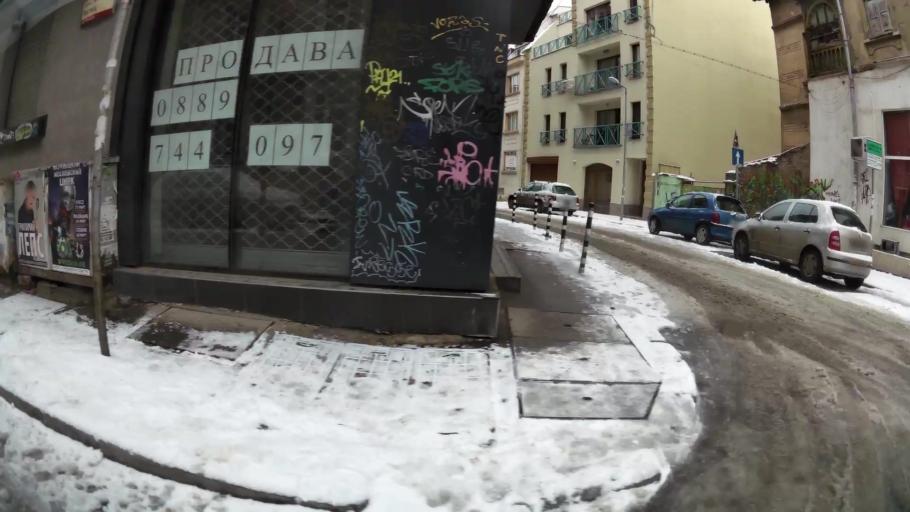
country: BG
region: Sofia-Capital
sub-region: Stolichna Obshtina
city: Sofia
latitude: 42.7035
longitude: 23.3255
